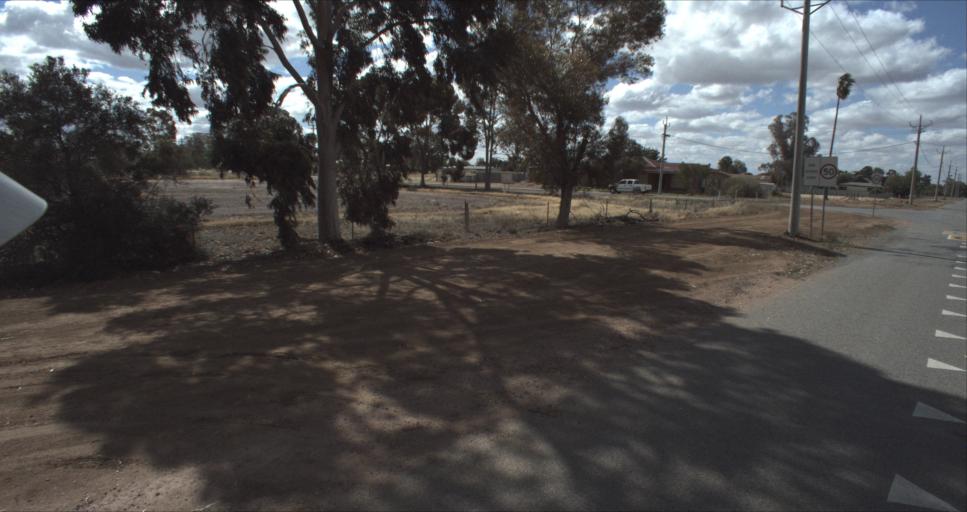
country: AU
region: New South Wales
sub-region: Leeton
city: Leeton
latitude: -34.5976
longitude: 146.4105
